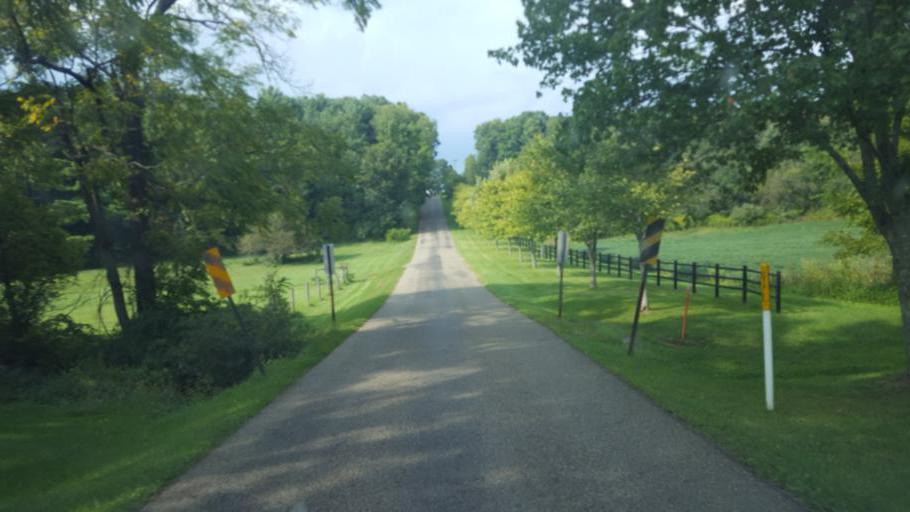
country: US
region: Ohio
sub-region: Knox County
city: Gambier
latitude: 40.3603
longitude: -82.4096
